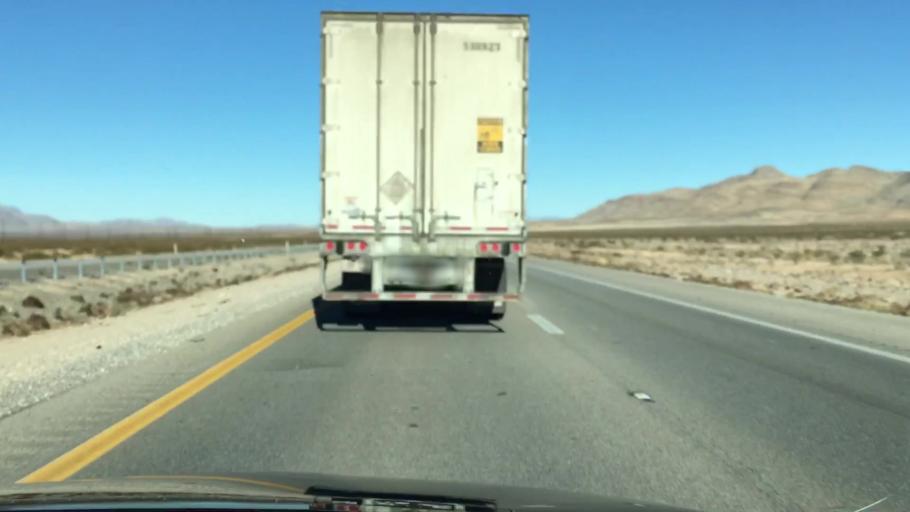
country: US
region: Nevada
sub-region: Clark County
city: Nellis Air Force Base
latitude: 36.4195
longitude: -114.8676
